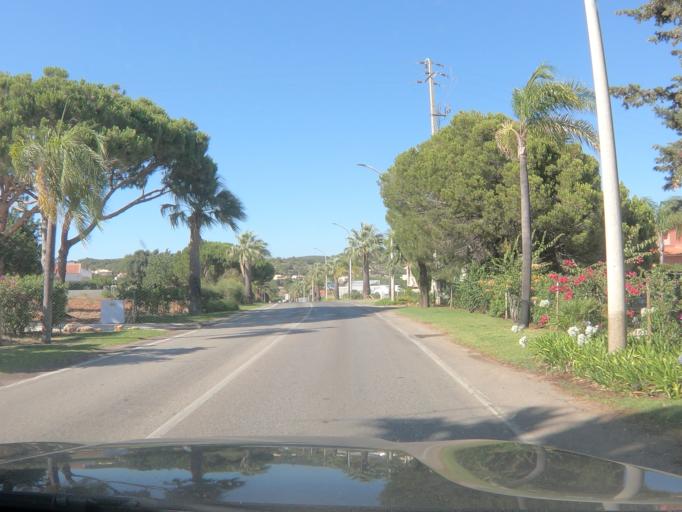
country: PT
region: Faro
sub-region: Loule
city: Vilamoura
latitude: 37.1124
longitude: -8.1191
